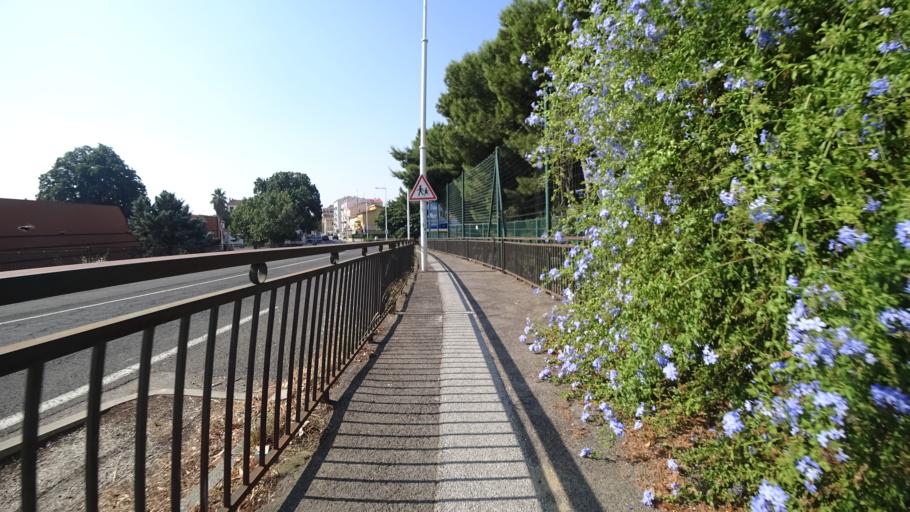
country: FR
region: Languedoc-Roussillon
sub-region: Departement des Pyrenees-Orientales
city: Perpignan
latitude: 42.7049
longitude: 2.8824
